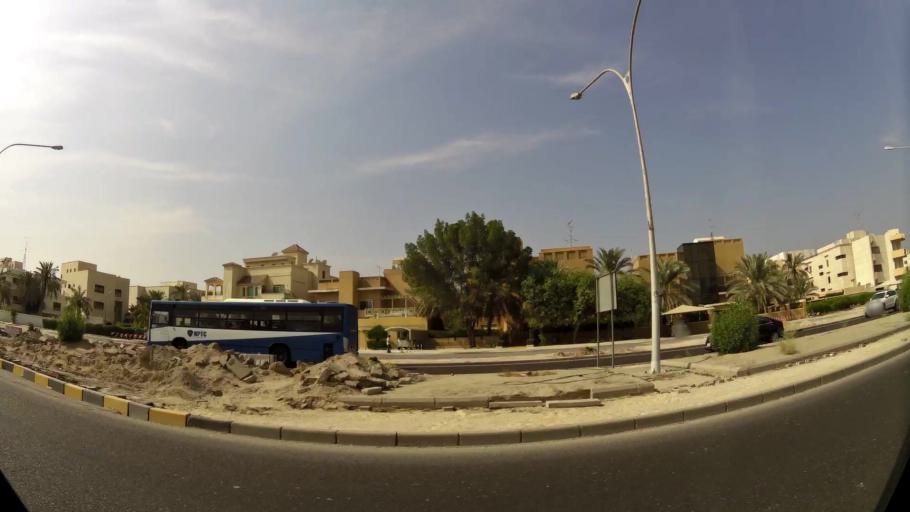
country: KW
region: Al Asimah
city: Ash Shamiyah
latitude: 29.3535
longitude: 47.9603
